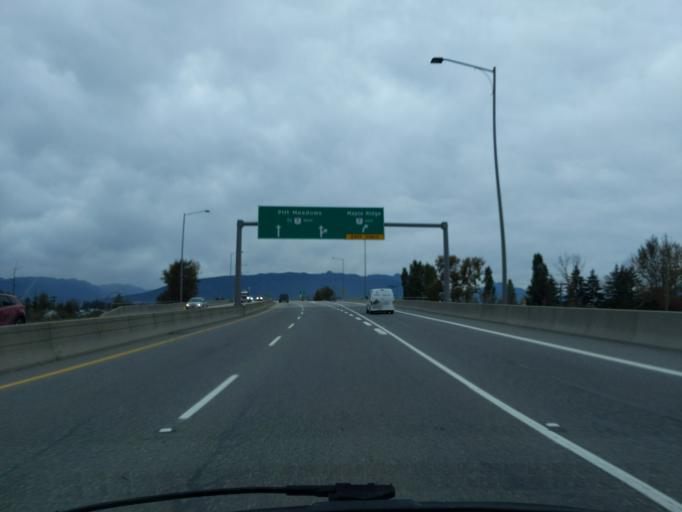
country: CA
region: British Columbia
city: Pitt Meadows
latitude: 49.2156
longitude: -122.6680
